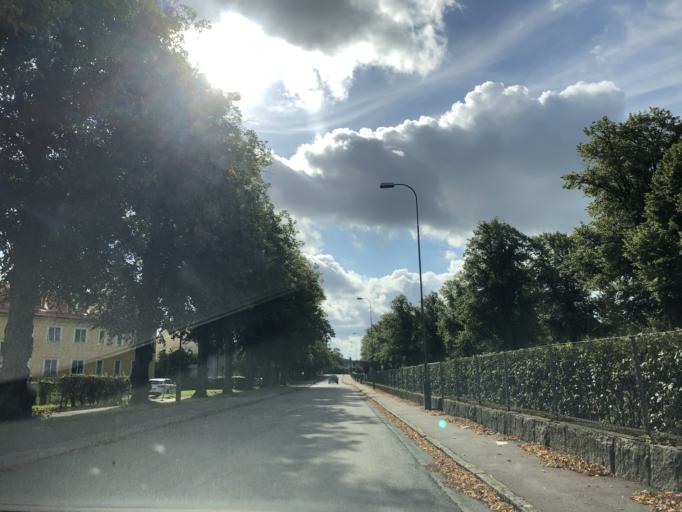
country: SE
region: Vaestra Goetaland
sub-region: Goteborg
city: Goeteborg
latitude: 57.7159
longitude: 12.0165
